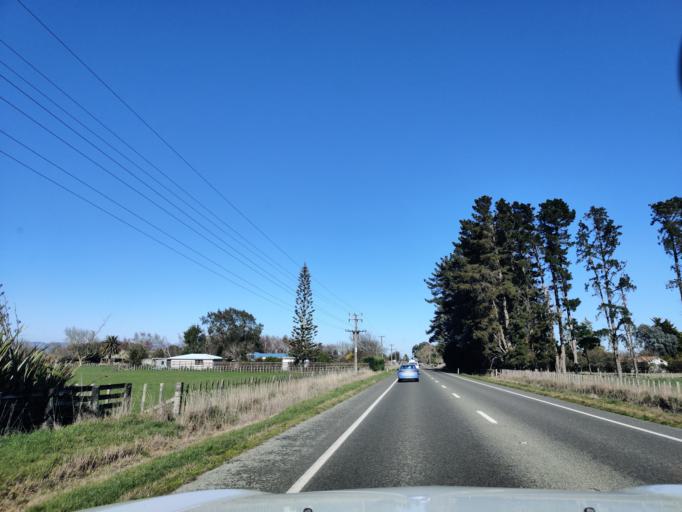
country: NZ
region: Manawatu-Wanganui
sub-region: Palmerston North City
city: Palmerston North
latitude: -40.2741
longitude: 175.5585
